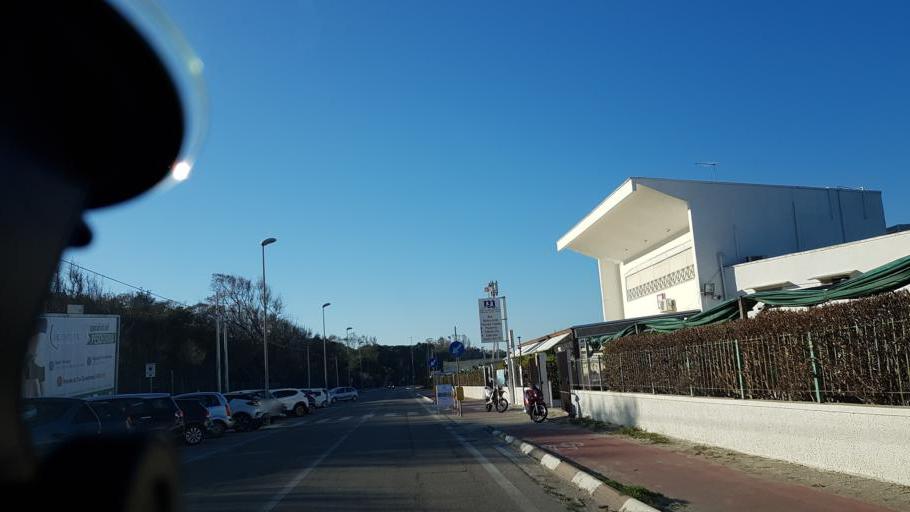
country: IT
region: Apulia
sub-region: Provincia di Lecce
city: Struda
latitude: 40.3817
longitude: 18.3066
